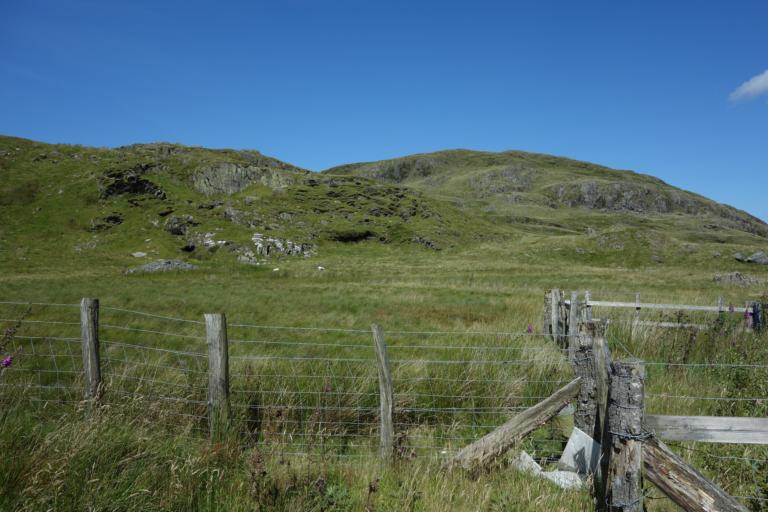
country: GB
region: Wales
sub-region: Gwynedd
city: Blaenau-Ffestiniog
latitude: 53.0194
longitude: -3.9394
